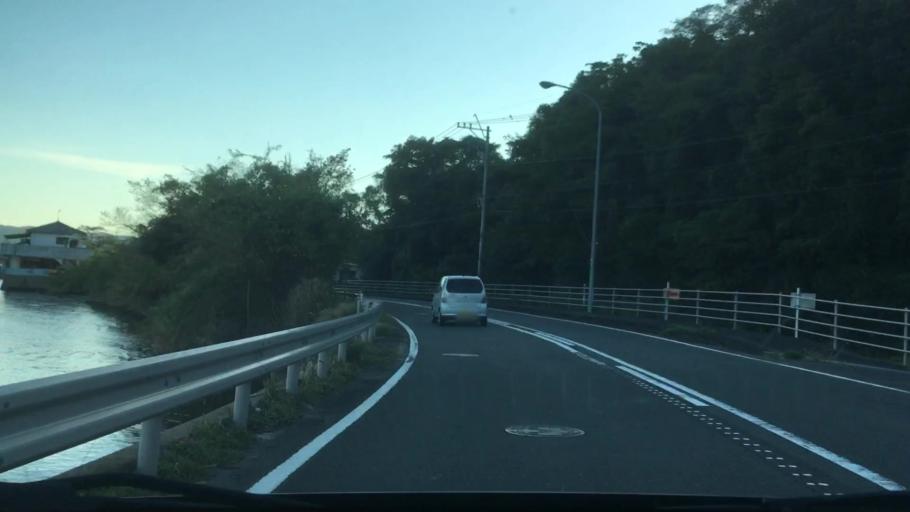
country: JP
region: Nagasaki
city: Sasebo
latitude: 33.0280
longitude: 129.7408
